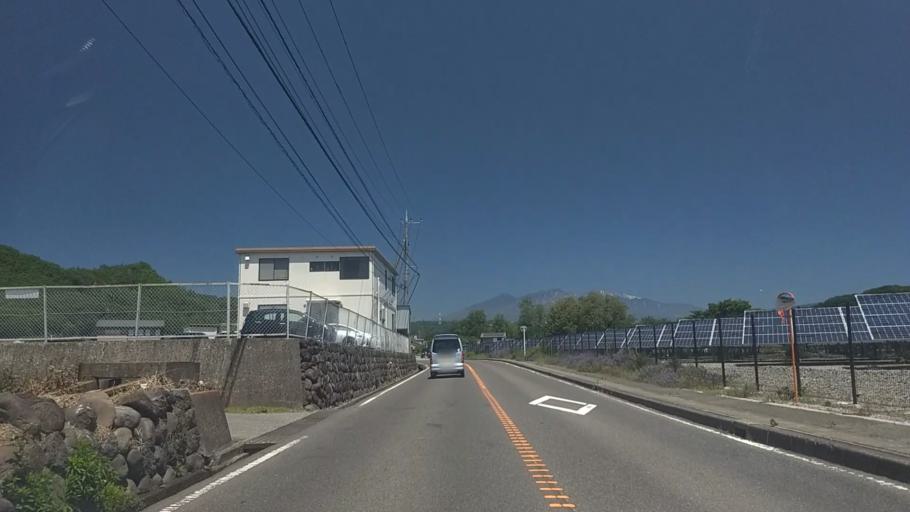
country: JP
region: Yamanashi
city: Nirasaki
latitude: 35.7629
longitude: 138.4288
